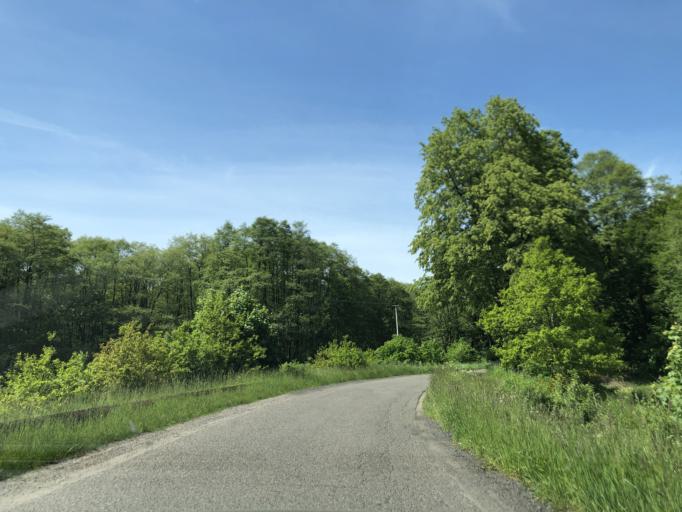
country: PL
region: West Pomeranian Voivodeship
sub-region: Powiat kolobrzeski
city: Dygowo
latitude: 54.0920
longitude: 15.7130
